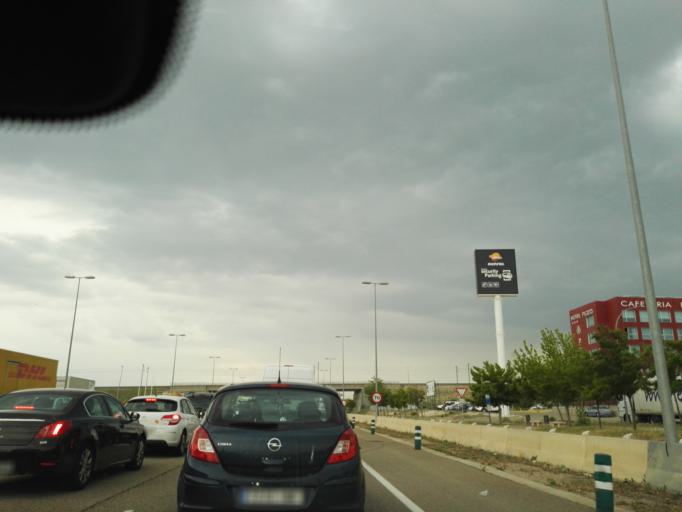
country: ES
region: Aragon
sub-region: Provincia de Zaragoza
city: Montecanal
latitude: 41.6361
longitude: -0.9905
